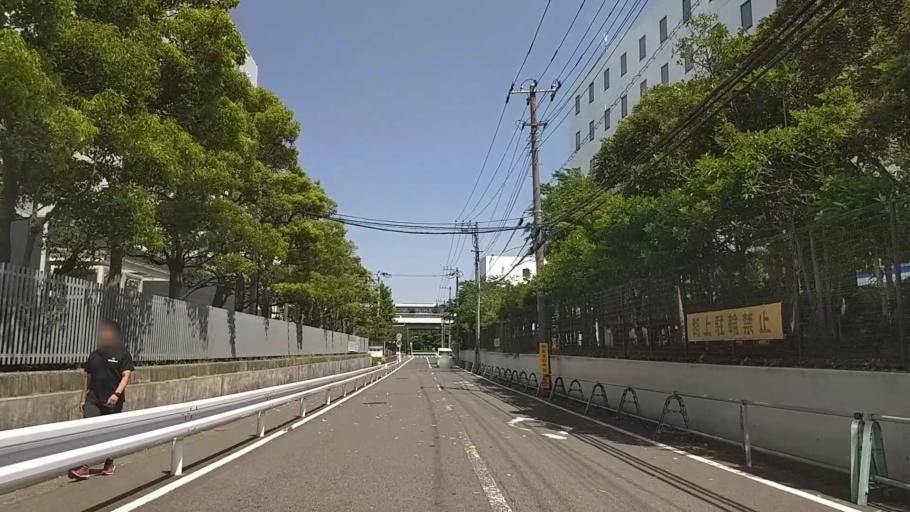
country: JP
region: Kanagawa
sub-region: Kawasaki-shi
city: Kawasaki
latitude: 35.4964
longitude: 139.6899
